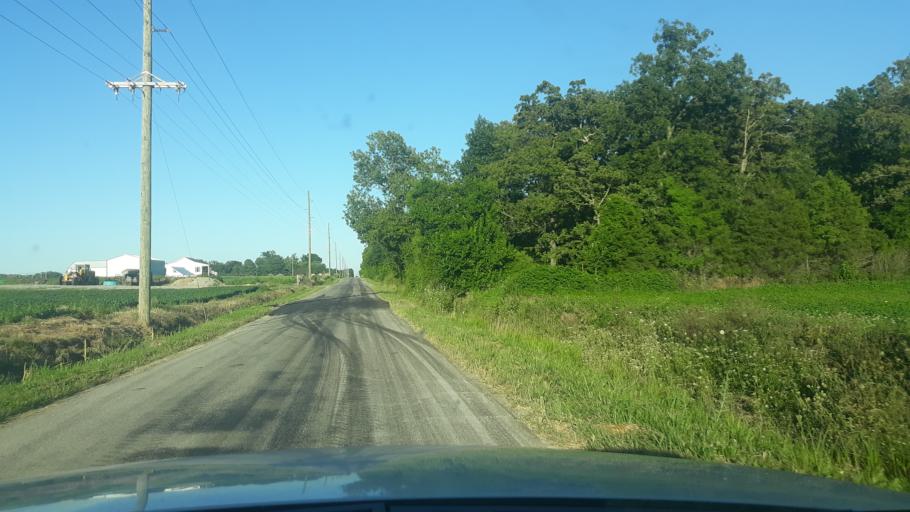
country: US
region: Illinois
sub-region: Saline County
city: Harrisburg
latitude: 37.8630
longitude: -88.5541
